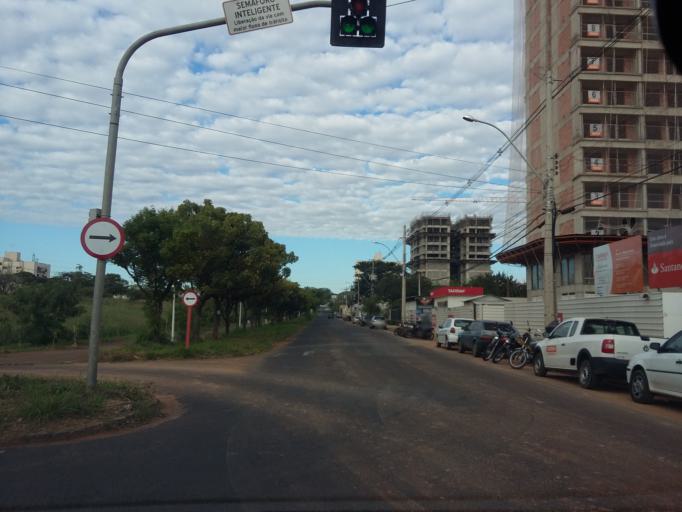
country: BR
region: Sao Paulo
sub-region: Sao Jose Do Rio Preto
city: Sao Jose do Rio Preto
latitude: -20.8382
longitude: -49.4095
